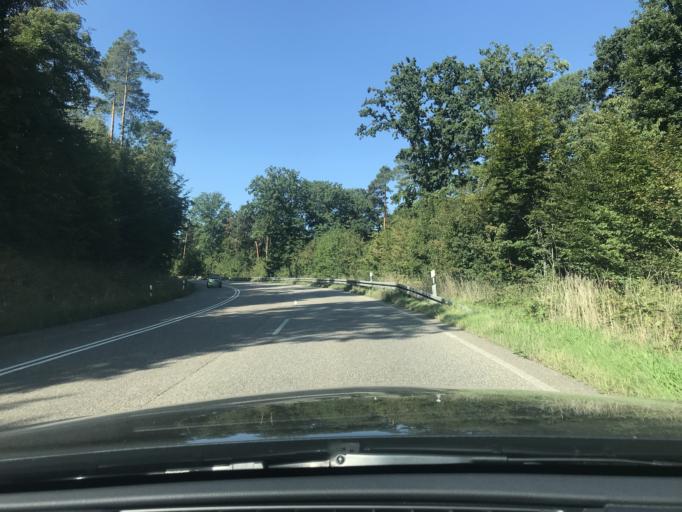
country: DE
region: Baden-Wuerttemberg
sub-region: Regierungsbezirk Stuttgart
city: Ostfildern
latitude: 48.7540
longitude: 9.2370
